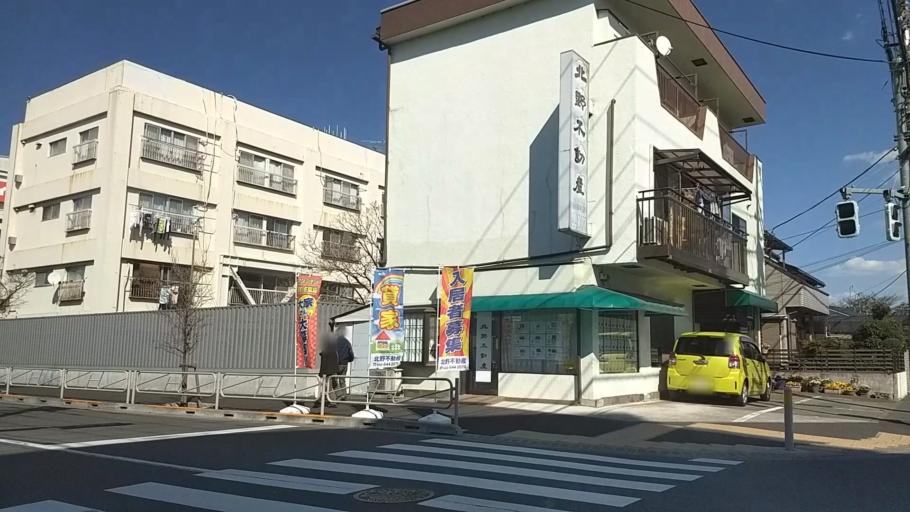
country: JP
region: Tokyo
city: Hachioji
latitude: 35.6467
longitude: 139.3548
